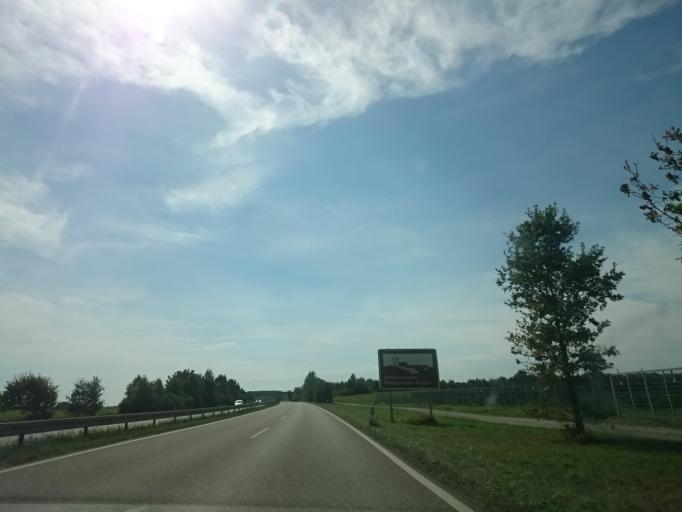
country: DE
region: Bavaria
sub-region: Swabia
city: Nordendorf
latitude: 48.6069
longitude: 10.8380
